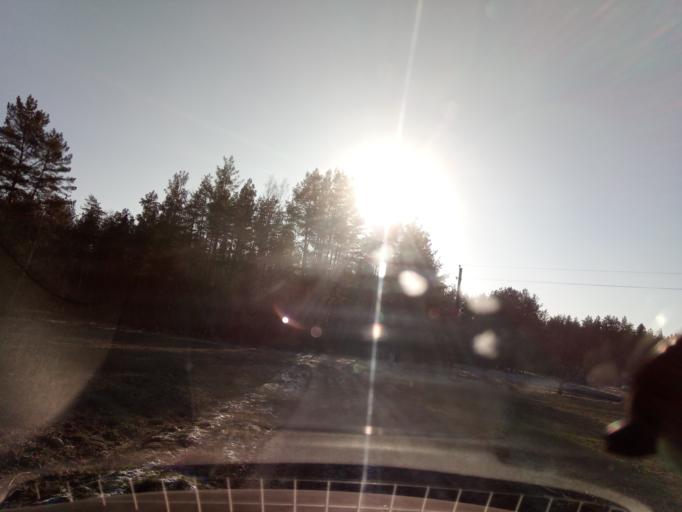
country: LT
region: Alytaus apskritis
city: Druskininkai
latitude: 53.9817
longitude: 23.8979
